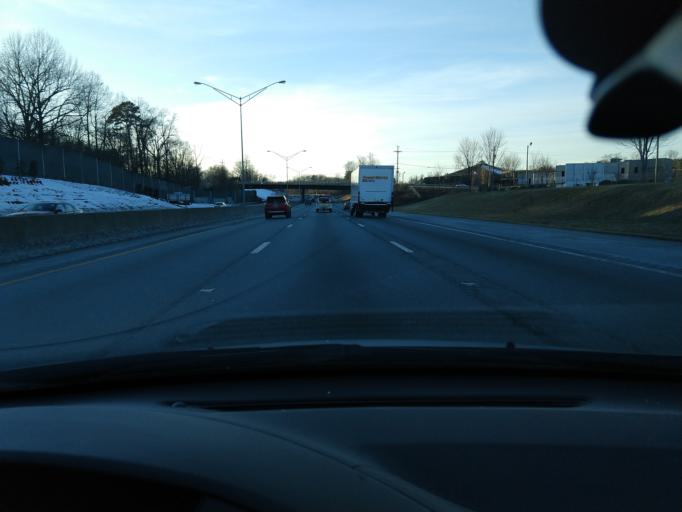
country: US
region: North Carolina
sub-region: Guilford County
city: Greensboro
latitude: 36.0477
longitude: -79.8542
